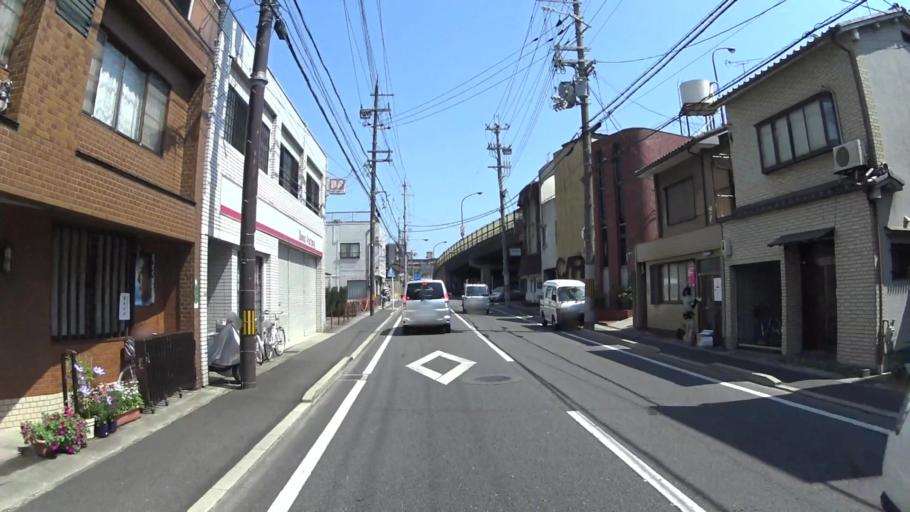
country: JP
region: Kyoto
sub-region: Kyoto-shi
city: Kamigyo-ku
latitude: 35.0559
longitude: 135.7916
